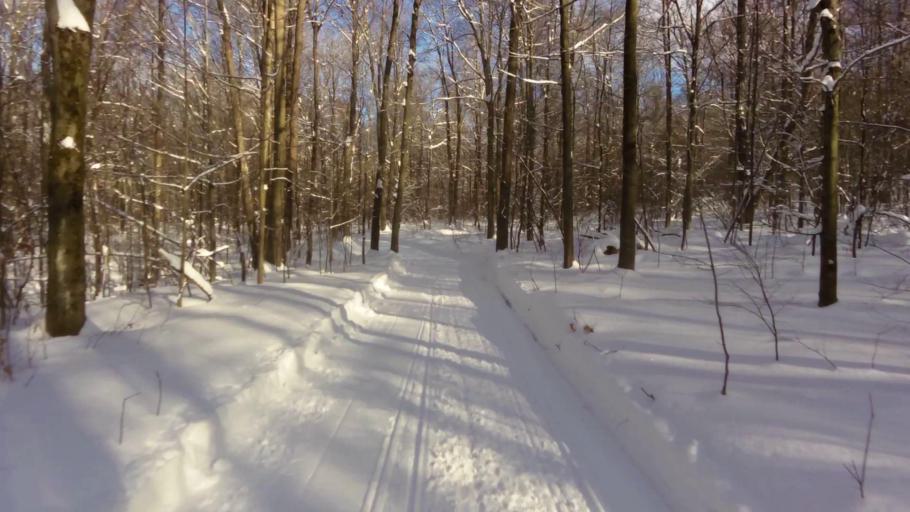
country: US
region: New York
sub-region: Chautauqua County
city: Falconer
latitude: 42.2574
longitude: -79.1431
